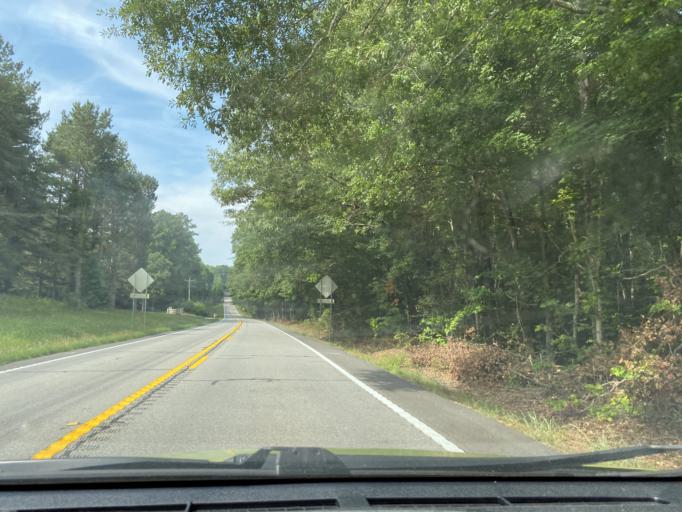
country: US
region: Georgia
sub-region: Coweta County
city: East Newnan
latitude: 33.2815
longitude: -84.7004
